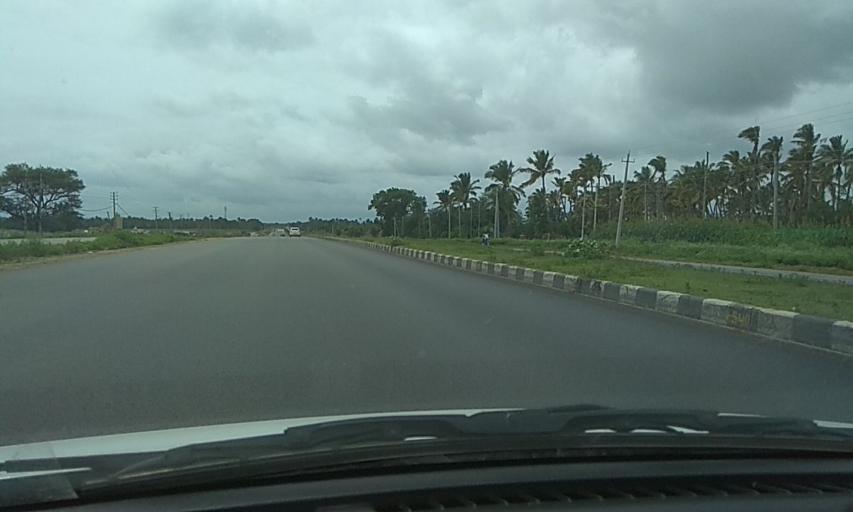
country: IN
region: Karnataka
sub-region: Davanagere
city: Mayakonda
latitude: 14.3545
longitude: 76.2002
